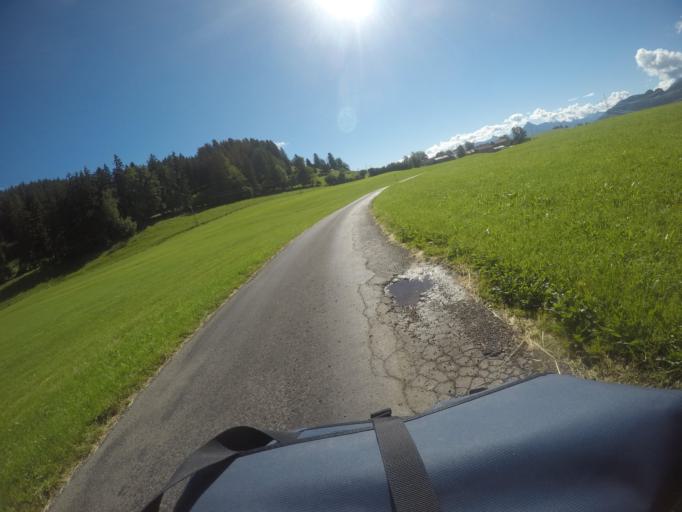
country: DE
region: Bavaria
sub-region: Swabia
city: Pfronten
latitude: 47.6069
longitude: 10.5529
